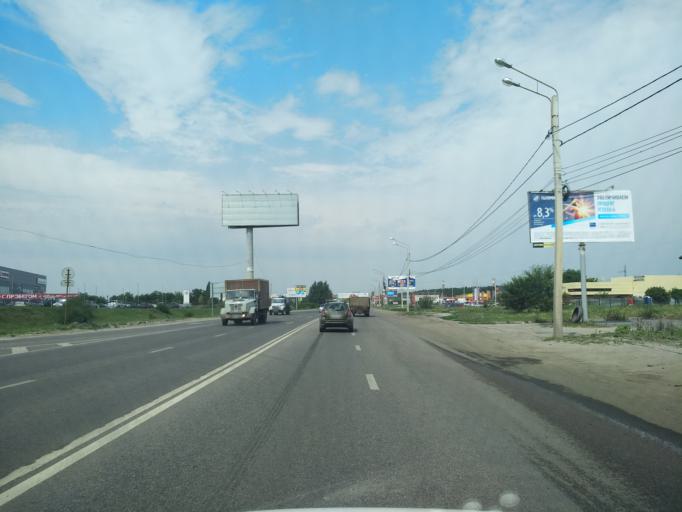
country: RU
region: Voronezj
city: Somovo
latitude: 51.6788
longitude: 39.2918
